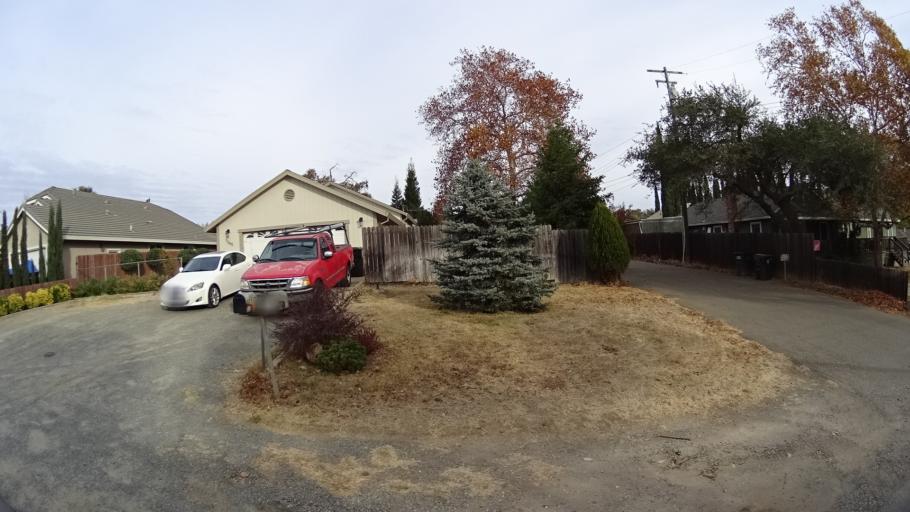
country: US
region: California
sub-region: Sacramento County
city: Citrus Heights
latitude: 38.7111
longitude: -121.2871
